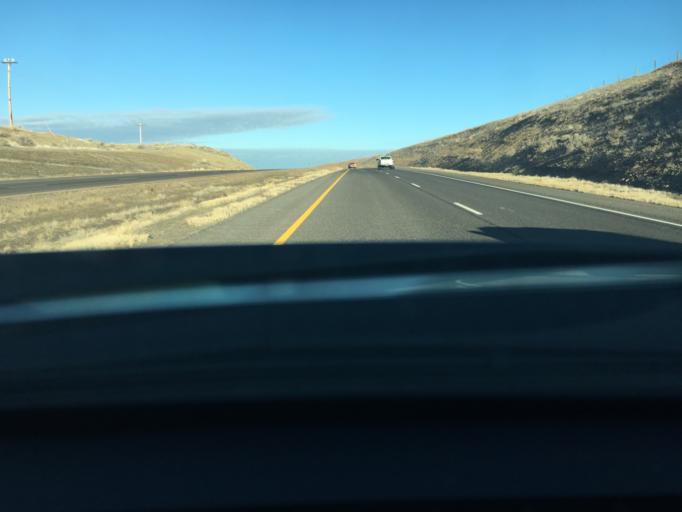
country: US
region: Colorado
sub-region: Mesa County
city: Clifton
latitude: 38.9227
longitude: -108.3816
